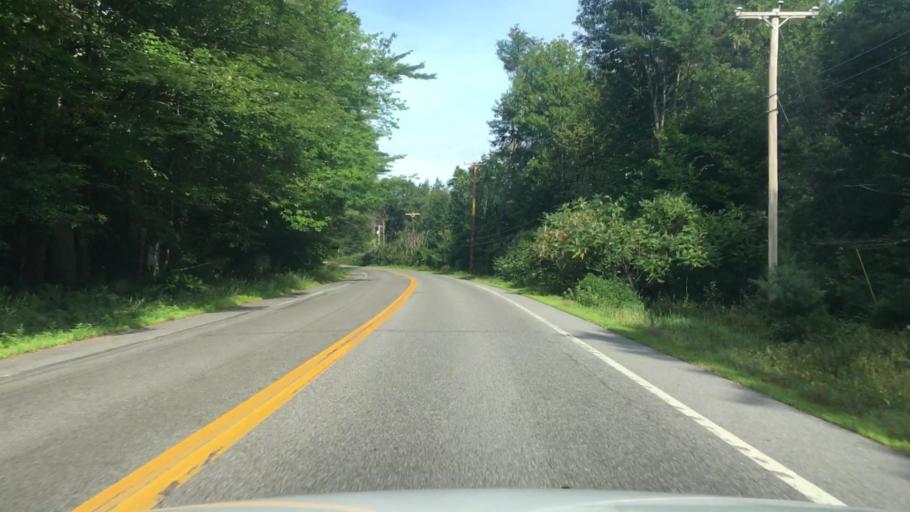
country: US
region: Maine
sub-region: York County
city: Cornish
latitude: 43.8057
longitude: -70.8363
